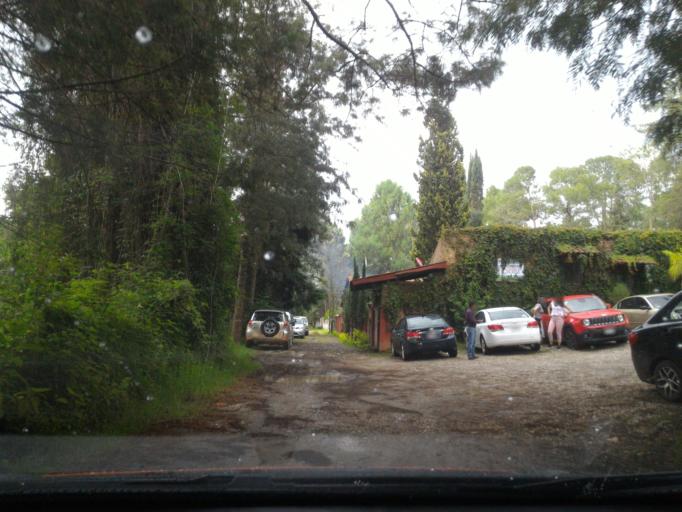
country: MX
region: Jalisco
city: San Andres Ixtlan
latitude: 19.8586
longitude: -103.4546
